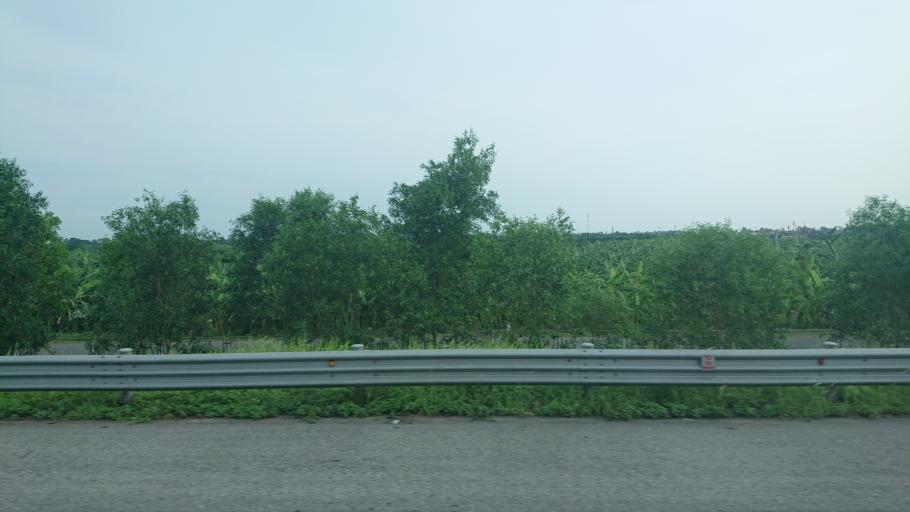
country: VN
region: Hai Duong
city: Tu Ky
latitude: 20.8290
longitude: 106.4530
